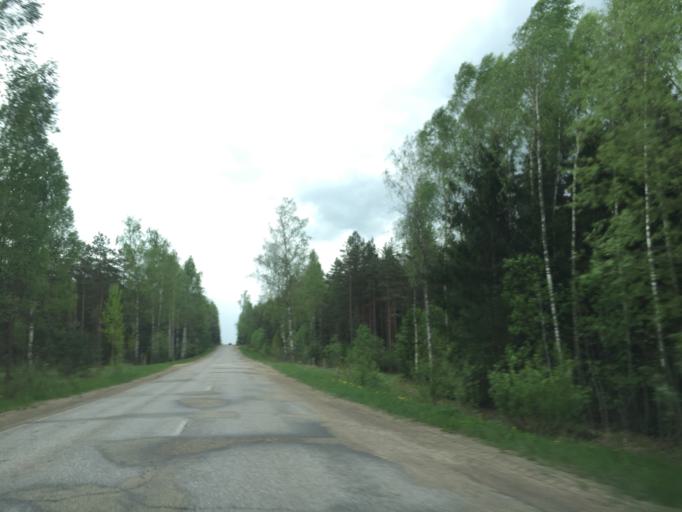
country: LV
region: Ogre
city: Ogre
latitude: 56.8477
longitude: 24.5715
